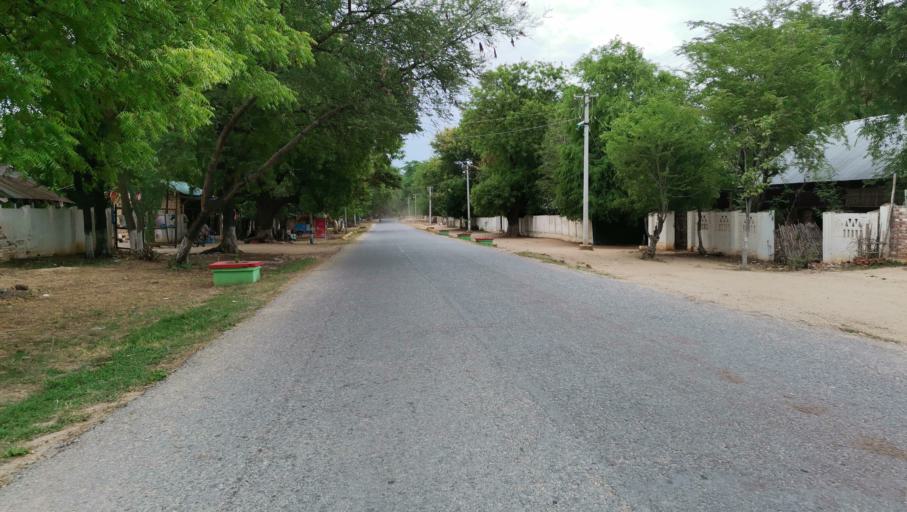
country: MM
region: Mandalay
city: Myingyan
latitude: 21.8410
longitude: 95.4268
